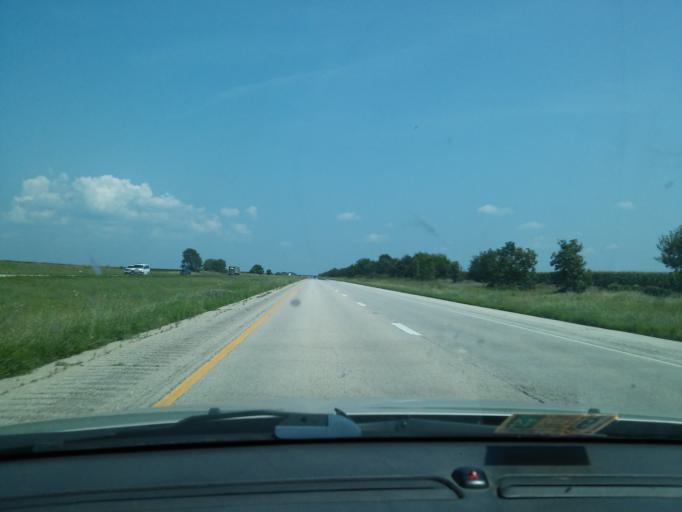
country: US
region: Illinois
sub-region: Sangamon County
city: New Berlin
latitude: 39.7406
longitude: -89.8677
